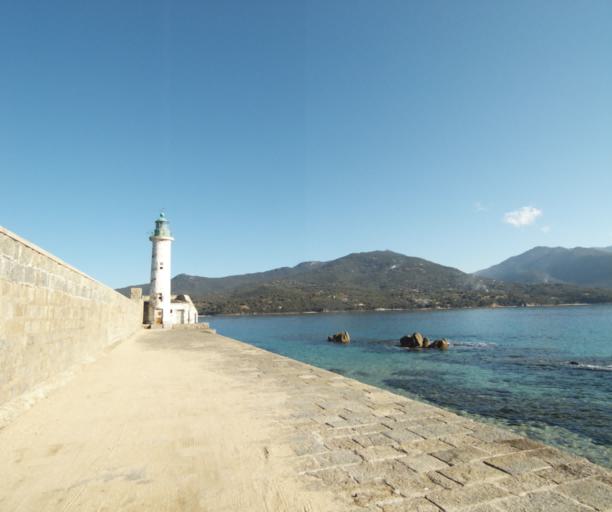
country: FR
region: Corsica
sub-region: Departement de la Corse-du-Sud
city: Propriano
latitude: 41.6781
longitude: 8.8975
